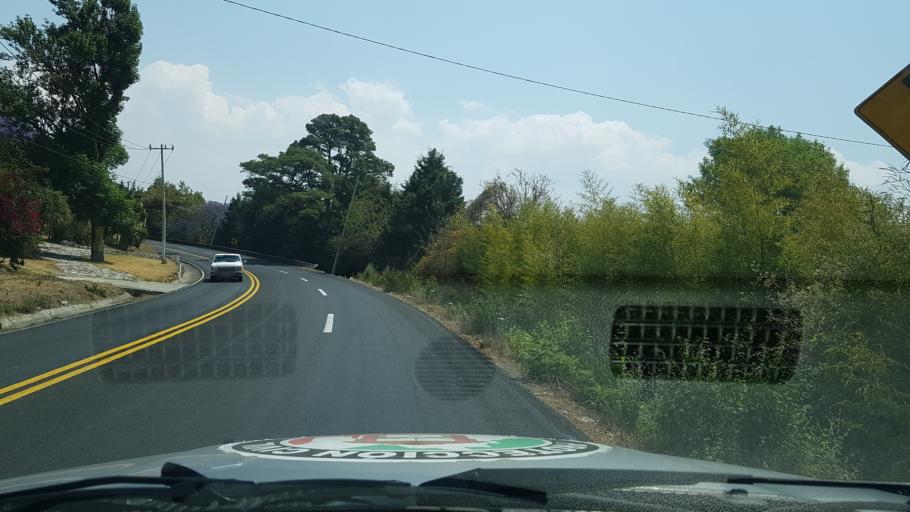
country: MX
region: Mexico
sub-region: Tepetlixpa
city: Nepantla de Sor Juana Ines de la Cruz
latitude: 18.9855
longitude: -98.8353
